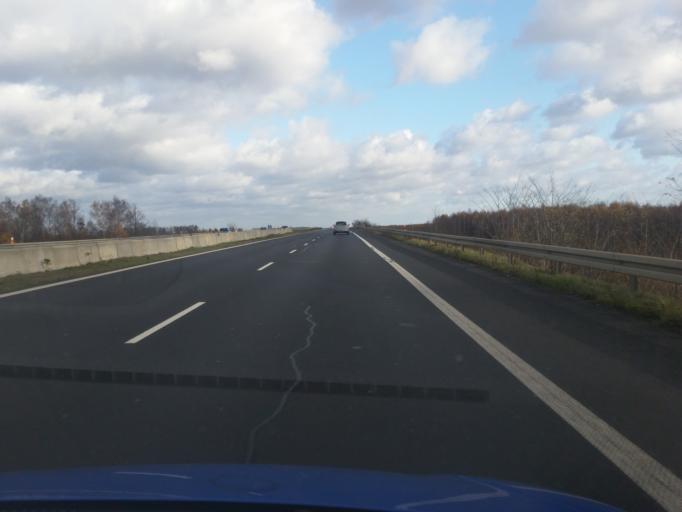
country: PL
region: Silesian Voivodeship
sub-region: Powiat czestochowski
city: Koscielec
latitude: 50.8894
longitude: 19.1779
